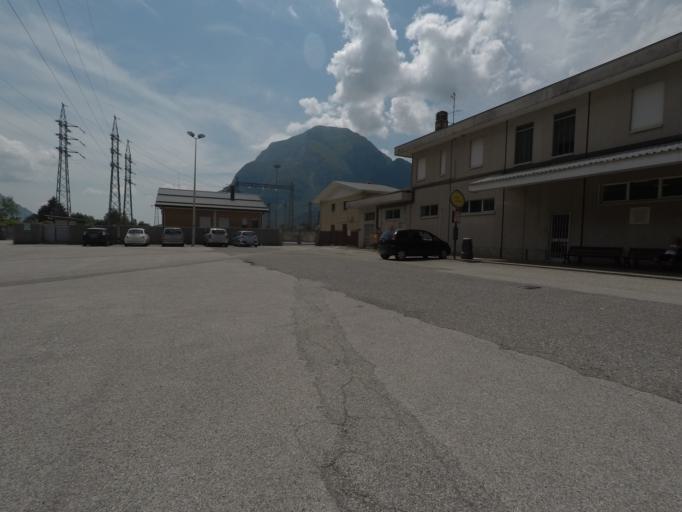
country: IT
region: Friuli Venezia Giulia
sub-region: Provincia di Udine
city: Amaro
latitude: 46.3737
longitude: 13.1334
